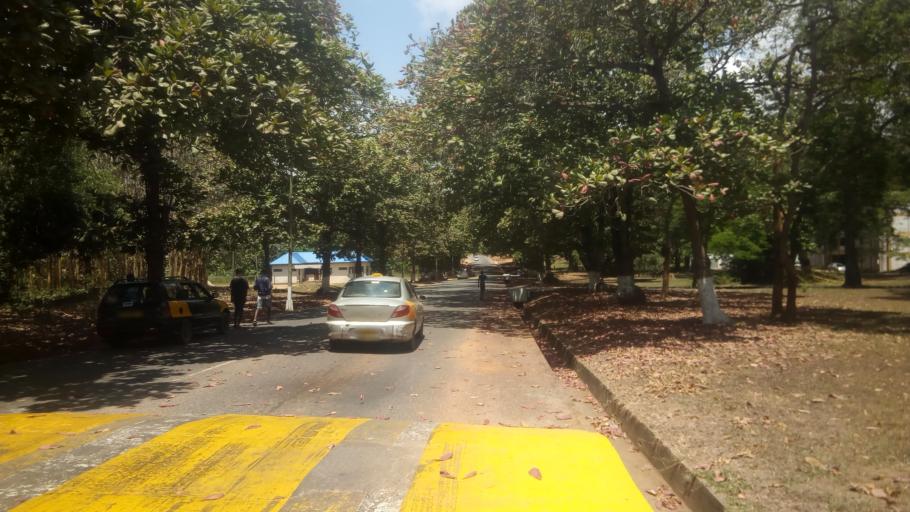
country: GH
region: Central
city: Cape Coast
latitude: 5.1073
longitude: -1.2851
